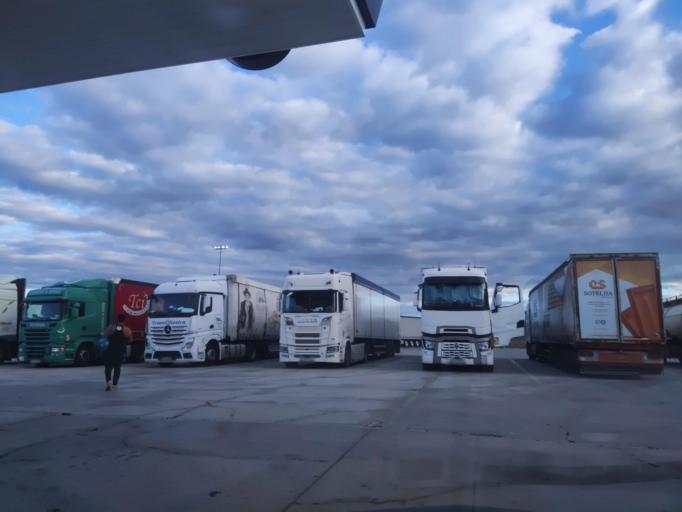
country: ES
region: Castille and Leon
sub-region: Provincia de Salamanca
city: Robliza de Cojos
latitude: 40.8780
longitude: -5.9829
